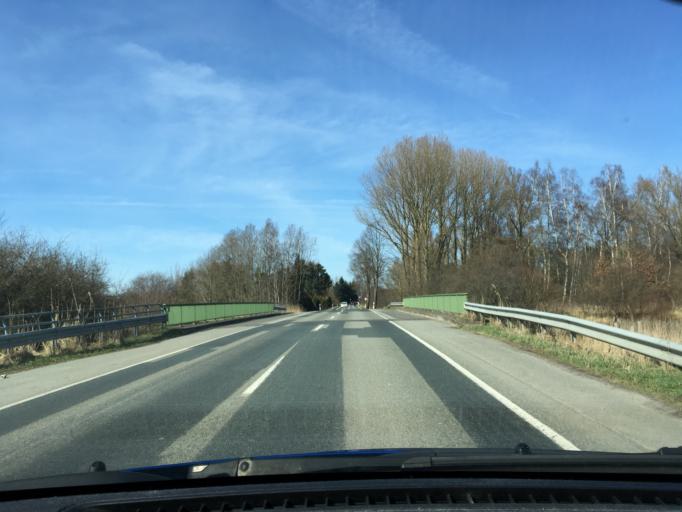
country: DE
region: Lower Saxony
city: Winsen
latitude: 53.3814
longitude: 10.2448
